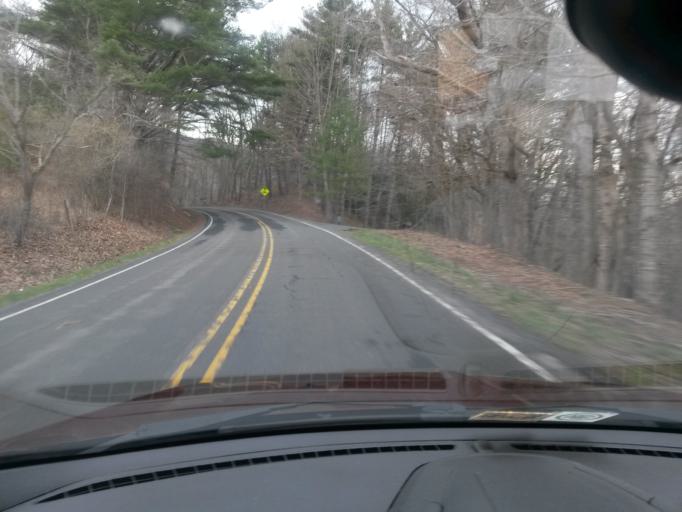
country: US
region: Virginia
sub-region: Bath County
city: Warm Springs
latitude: 38.1745
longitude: -79.7389
